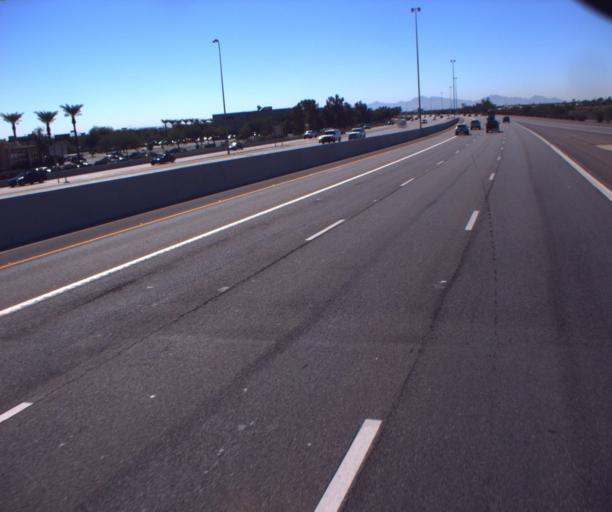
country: US
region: Arizona
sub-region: Maricopa County
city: Sun City
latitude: 33.6340
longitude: -112.2394
